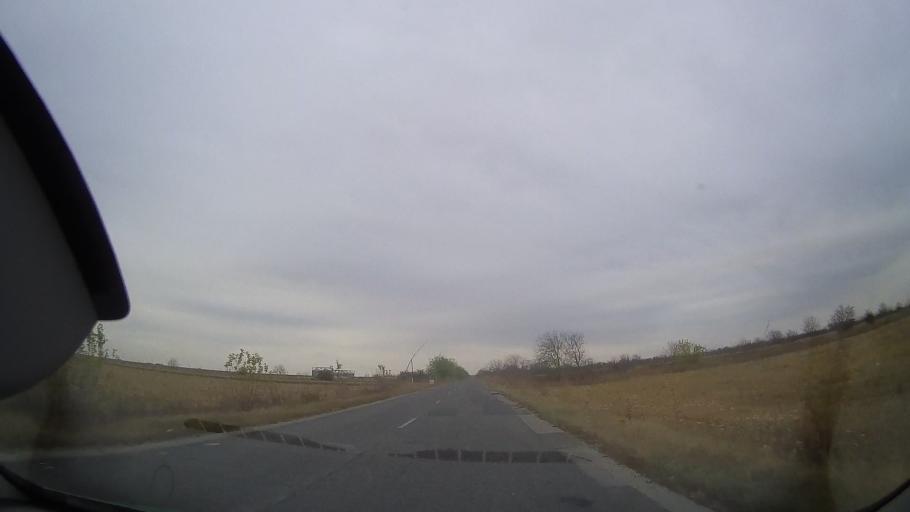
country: RO
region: Ialomita
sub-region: Comuna Milosesti
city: Milosesti
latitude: 44.7535
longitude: 27.2174
